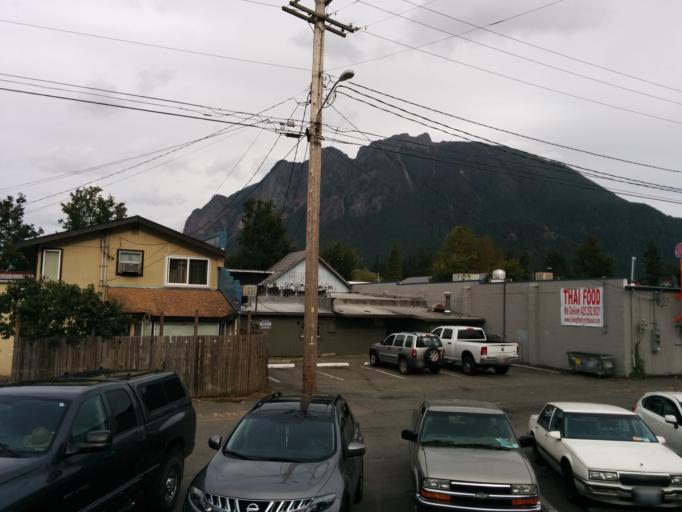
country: US
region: Washington
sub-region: King County
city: North Bend
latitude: 47.4943
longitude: -121.7859
